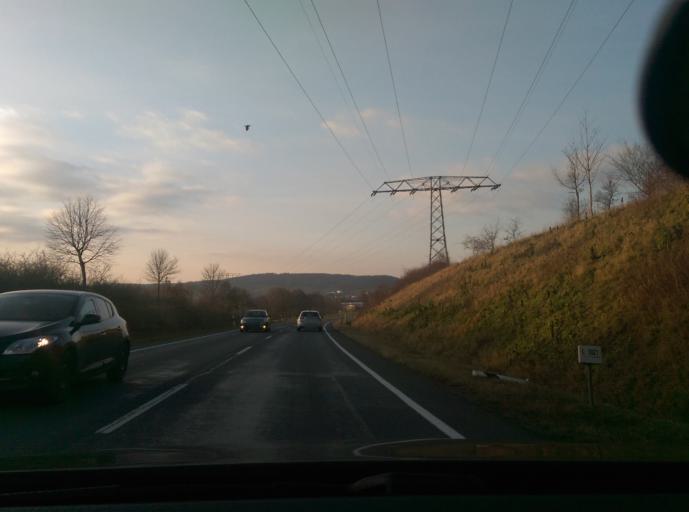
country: DE
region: Thuringia
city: Eisenach
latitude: 50.9974
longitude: 10.3385
